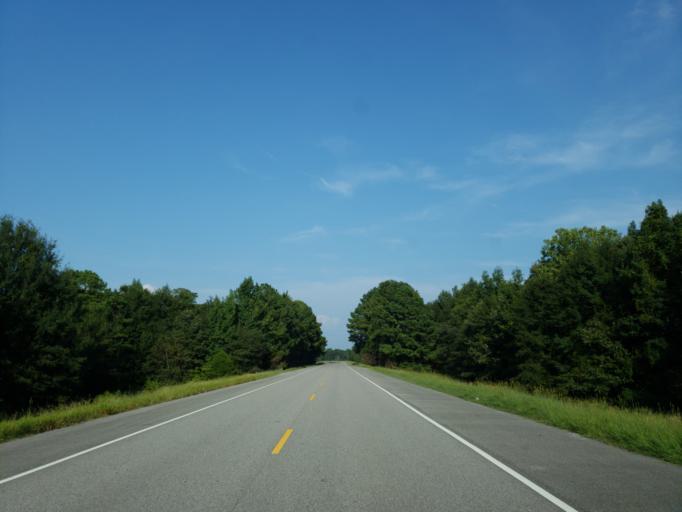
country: US
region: Alabama
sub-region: Sumter County
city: Livingston
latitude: 32.6979
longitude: -88.1035
